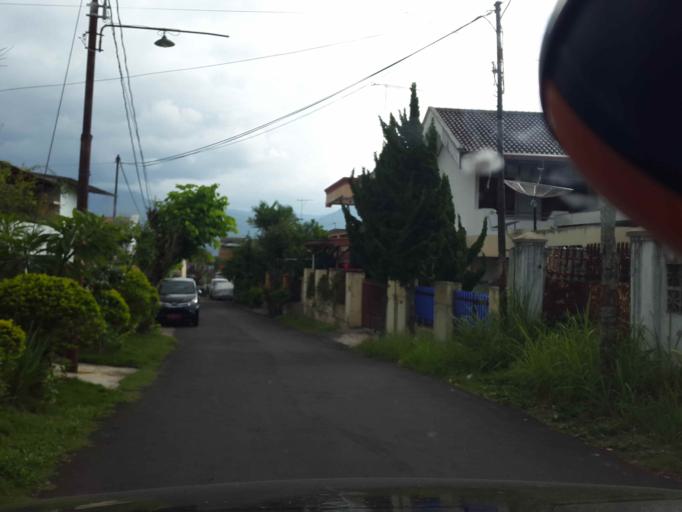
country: ID
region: Central Java
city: Salatiga
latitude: -7.3149
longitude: 110.4930
